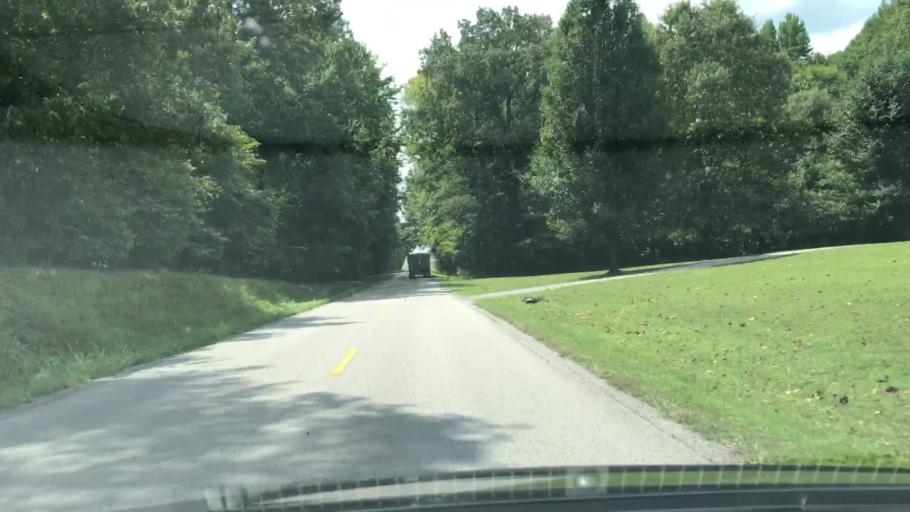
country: US
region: Kentucky
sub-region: Todd County
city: Guthrie
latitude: 36.6669
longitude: -87.0250
